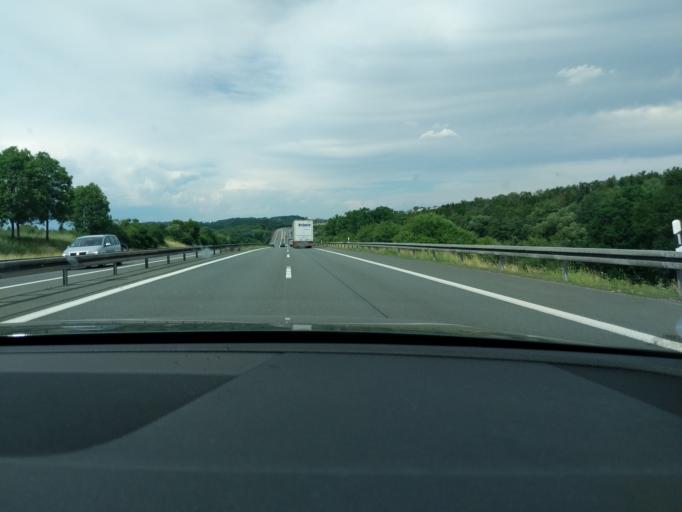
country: DE
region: Saxony
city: Neuensalz
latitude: 50.4805
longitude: 12.1856
